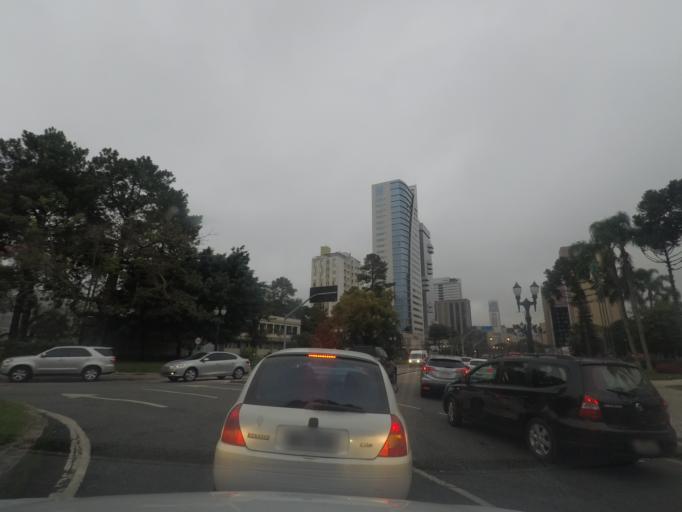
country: BR
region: Parana
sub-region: Curitiba
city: Curitiba
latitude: -25.4166
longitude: -49.2684
